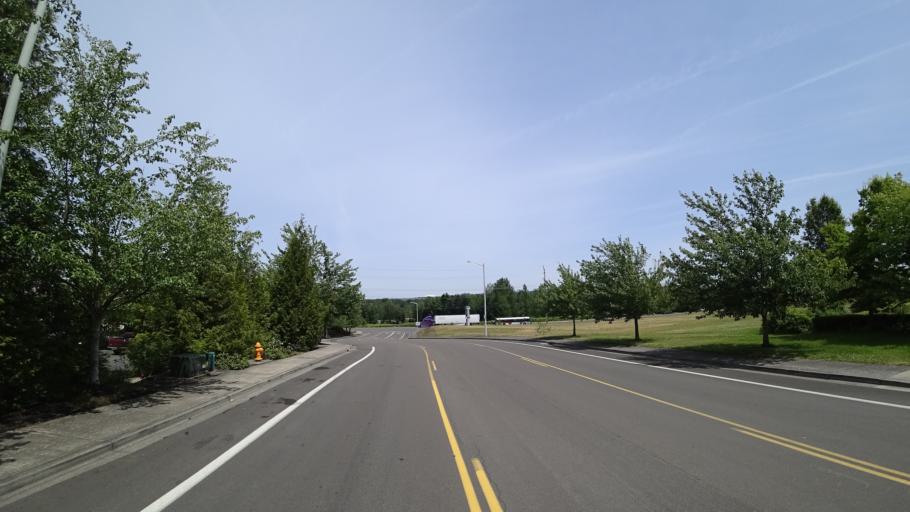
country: US
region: Oregon
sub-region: Multnomah County
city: Fairview
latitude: 45.5464
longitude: -122.4857
